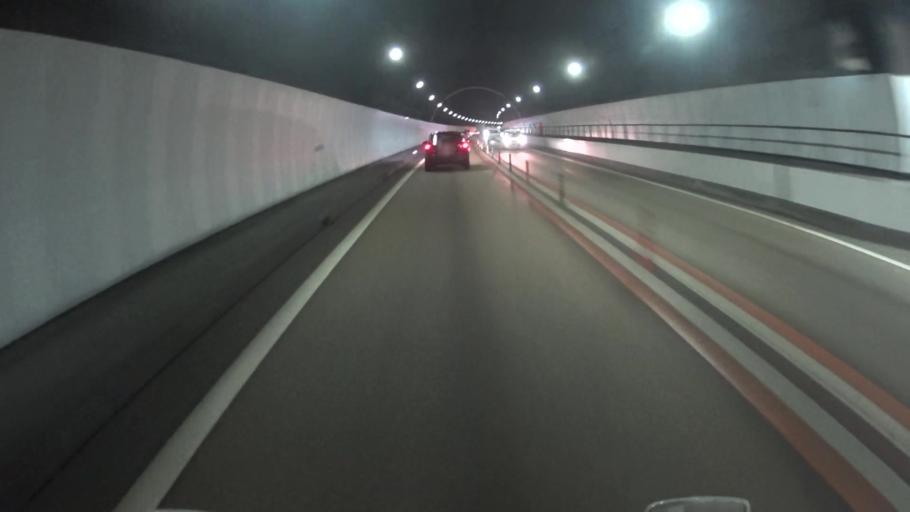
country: JP
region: Kyoto
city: Kameoka
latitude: 35.1378
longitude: 135.4513
